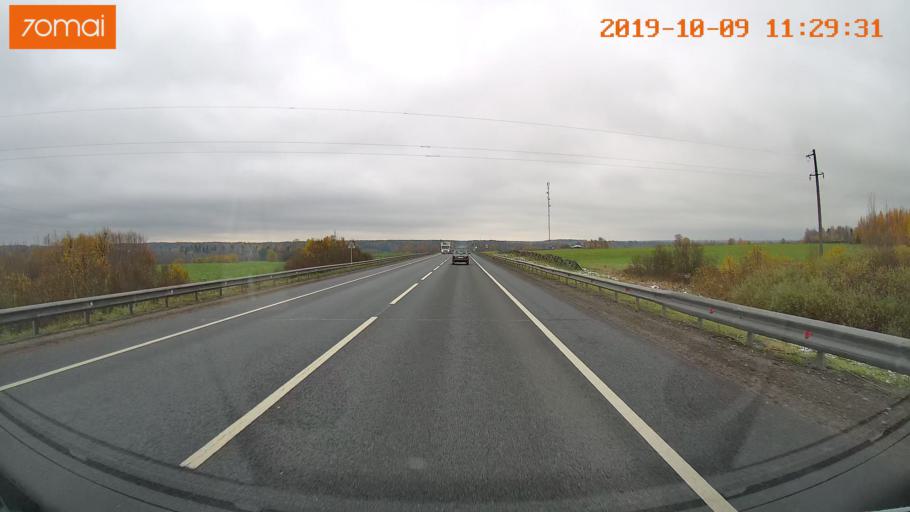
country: RU
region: Vologda
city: Vologda
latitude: 59.0613
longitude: 40.0557
